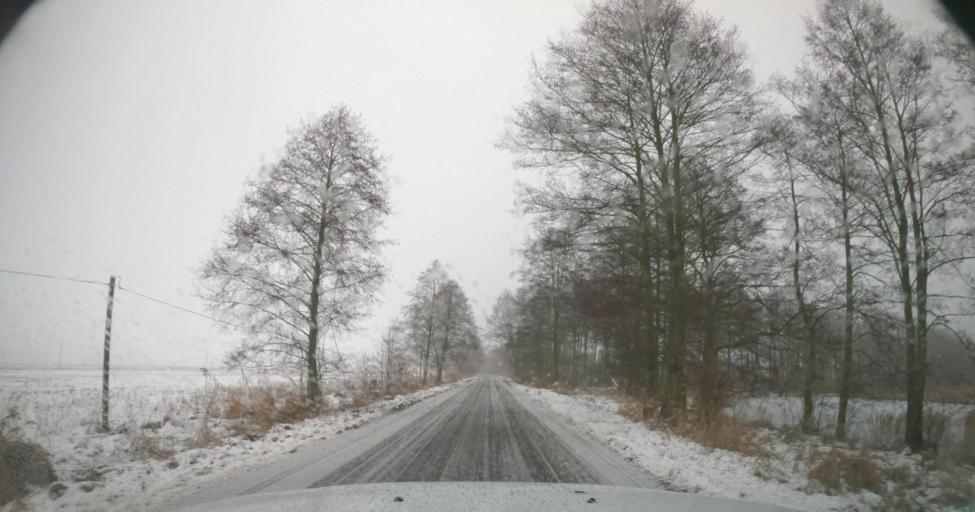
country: PL
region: West Pomeranian Voivodeship
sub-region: Powiat policki
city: Police
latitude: 53.5594
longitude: 14.6527
